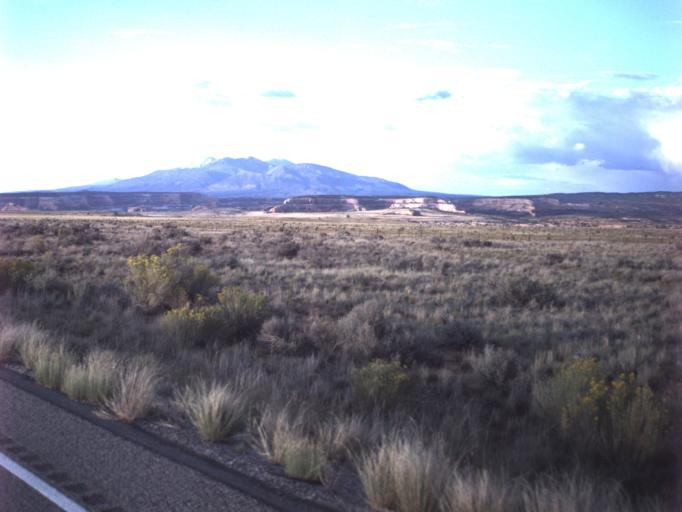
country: US
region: Utah
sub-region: San Juan County
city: Monticello
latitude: 38.1626
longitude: -109.3770
